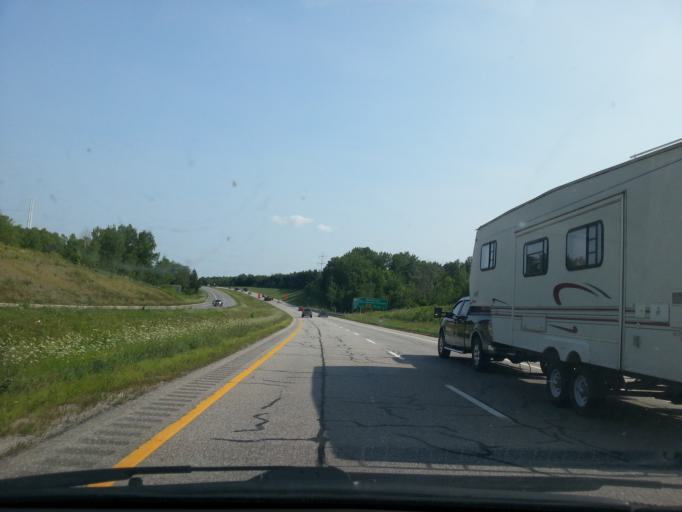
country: CA
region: Quebec
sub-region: Outaouais
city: Gatineau
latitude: 45.4862
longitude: -75.7963
